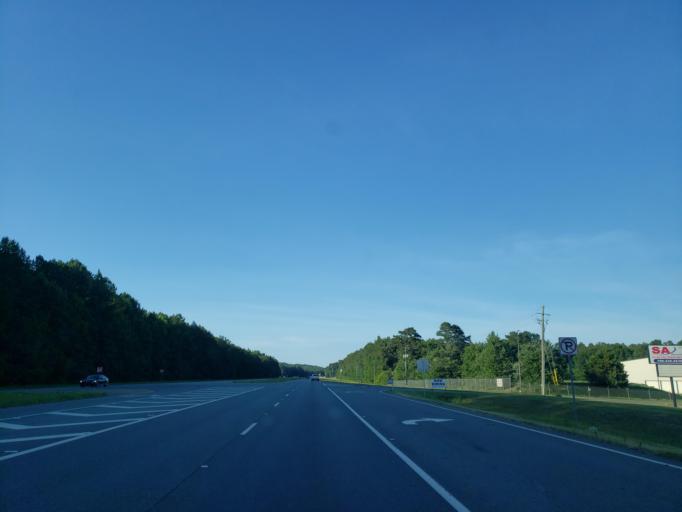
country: US
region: Georgia
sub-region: Floyd County
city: Shannon
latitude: 34.3201
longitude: -85.1045
